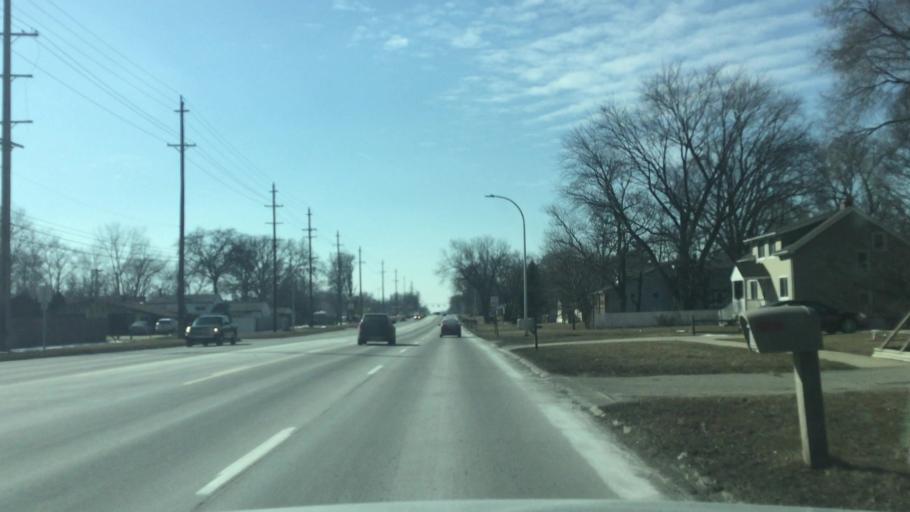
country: US
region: Michigan
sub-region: Wayne County
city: Westland
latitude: 42.3101
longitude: -83.3813
